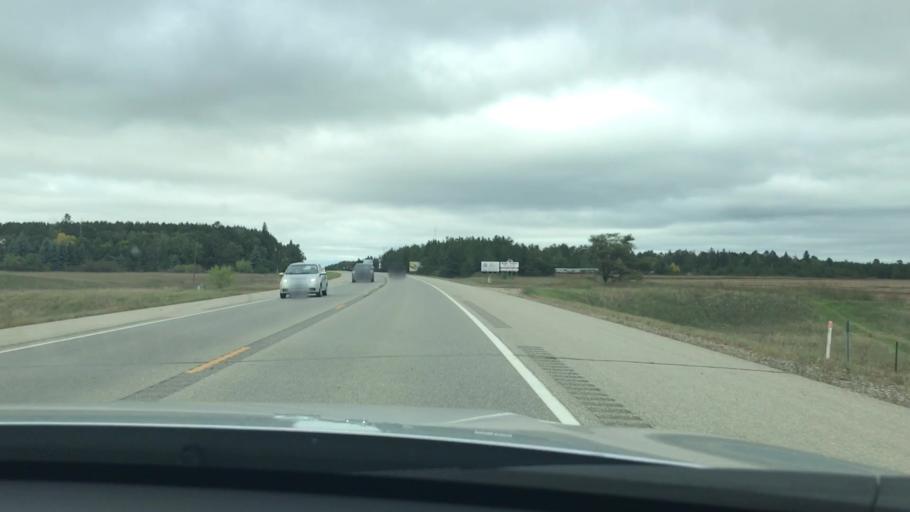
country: US
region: Minnesota
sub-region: Hubbard County
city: Park Rapids
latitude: 46.8674
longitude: -95.0679
